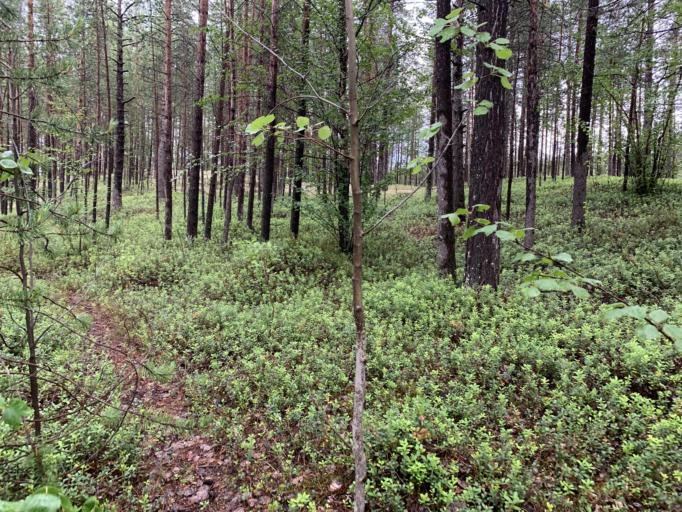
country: RU
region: Murmansk
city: Monchegorsk
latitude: 67.9538
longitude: 33.0253
